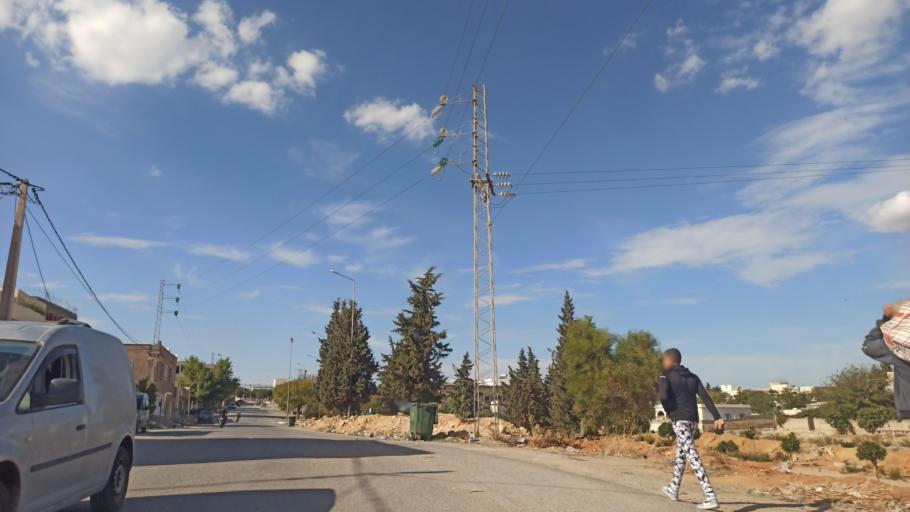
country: TN
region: Zaghwan
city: Zaghouan
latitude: 36.3472
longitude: 10.2075
